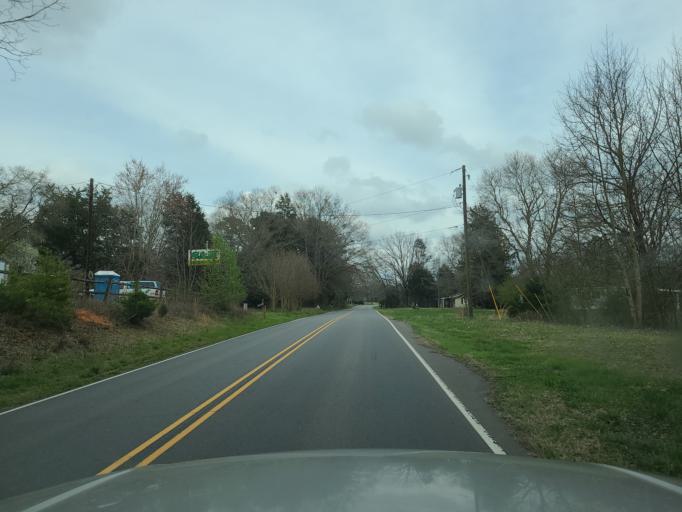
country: US
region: North Carolina
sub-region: Cleveland County
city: Boiling Springs
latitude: 35.2554
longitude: -81.6897
